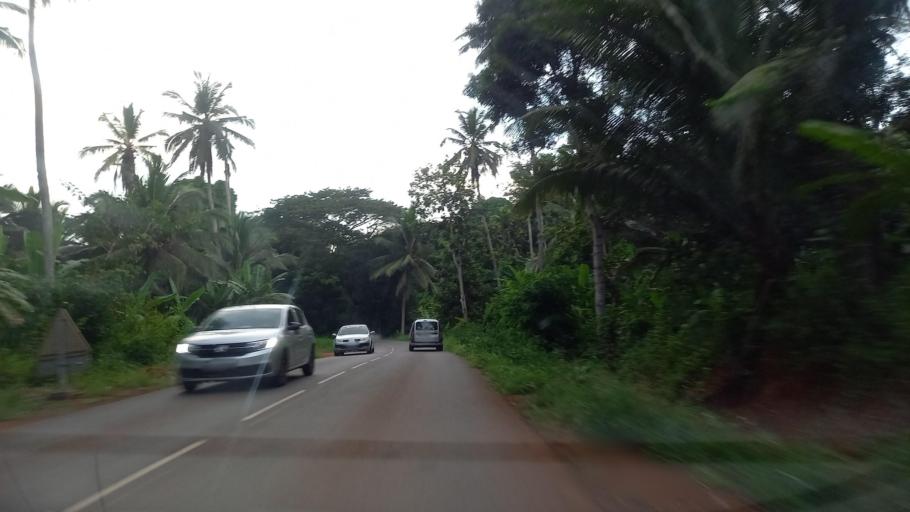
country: YT
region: M'Tsangamouji
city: M'Tsangamouji
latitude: -12.7580
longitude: 45.0960
